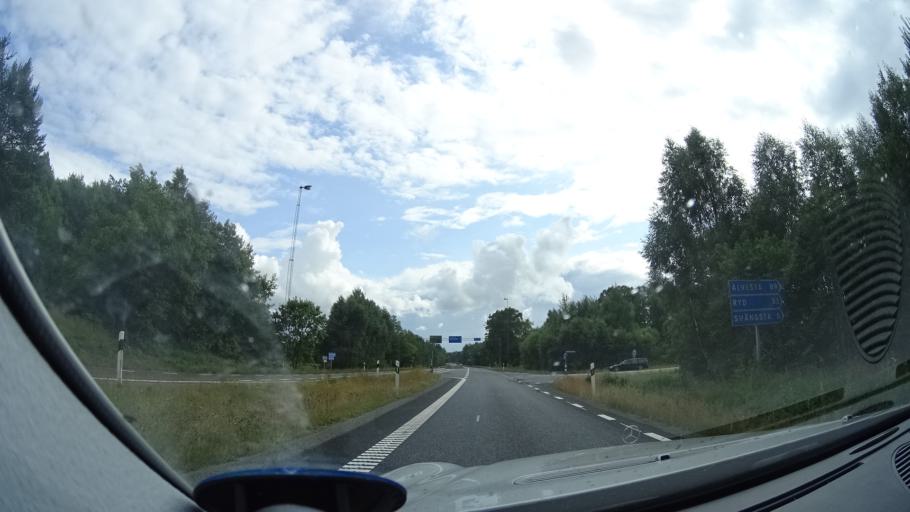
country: SE
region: Blekinge
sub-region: Karlshamns Kommun
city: Svangsta
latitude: 56.2269
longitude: 14.8206
